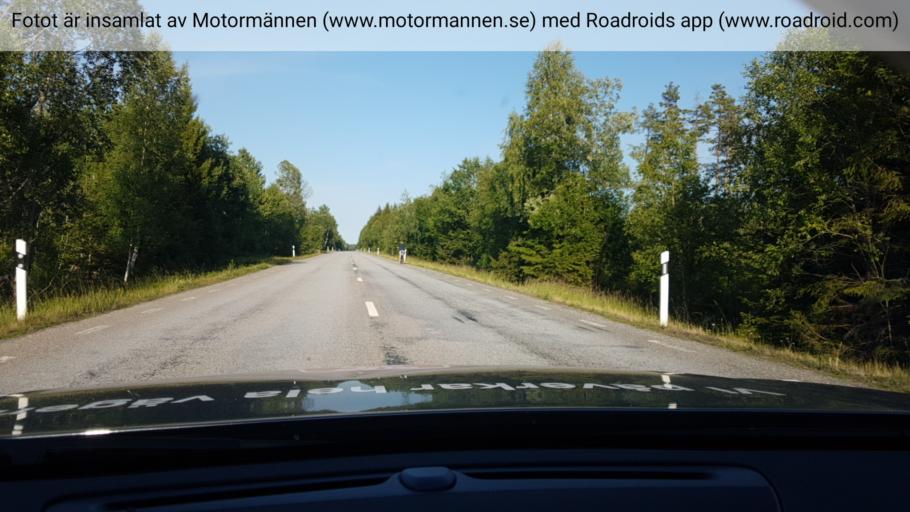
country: SE
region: Uppsala
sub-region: Osthammars Kommun
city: Gimo
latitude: 60.1650
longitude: 18.1409
